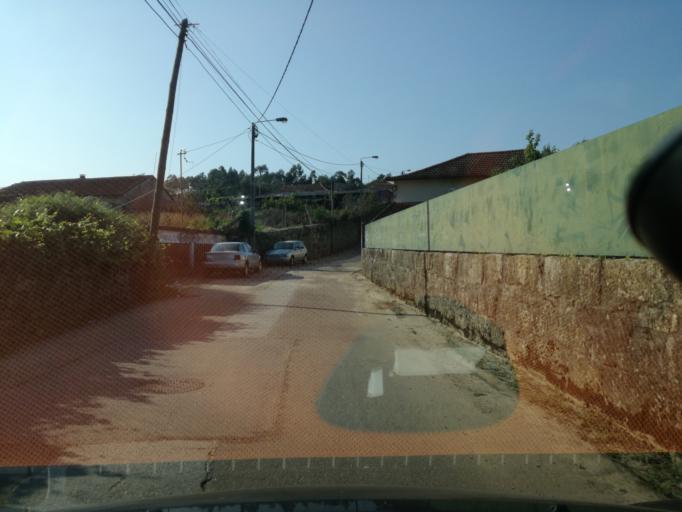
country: PT
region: Porto
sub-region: Maia
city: Anta
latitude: 41.2712
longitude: -8.6212
